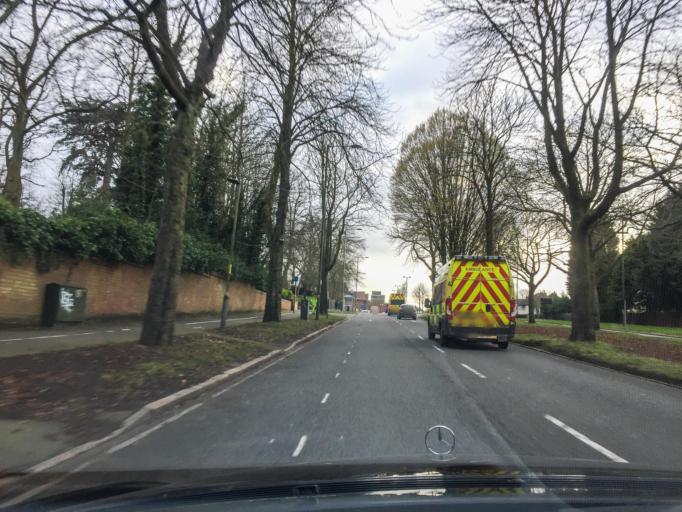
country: GB
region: England
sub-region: City and Borough of Birmingham
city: Bartley Green
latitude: 52.4201
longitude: -1.9633
